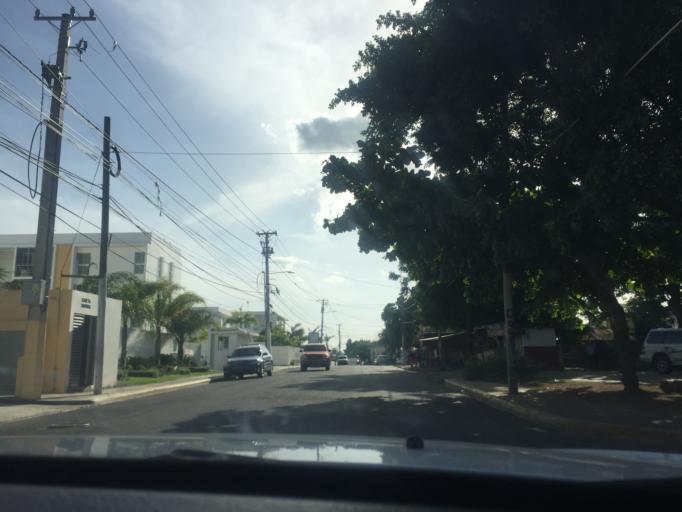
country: DO
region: Santiago
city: Tamboril
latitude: 19.4700
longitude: -70.6487
